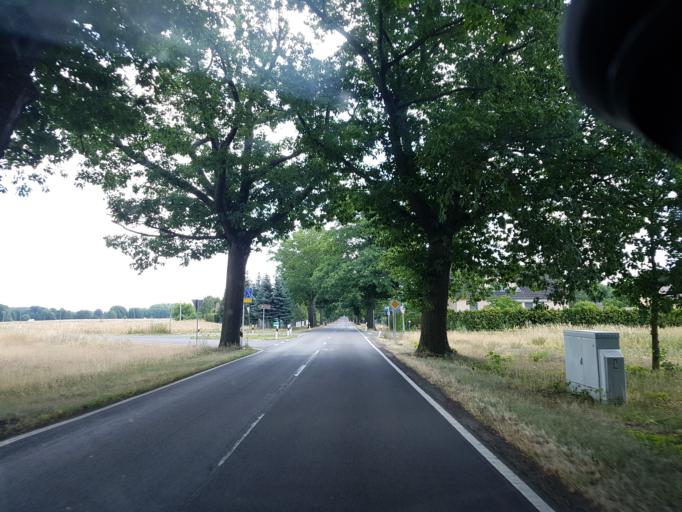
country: DE
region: Brandenburg
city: Drebkau
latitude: 51.6620
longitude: 14.2017
